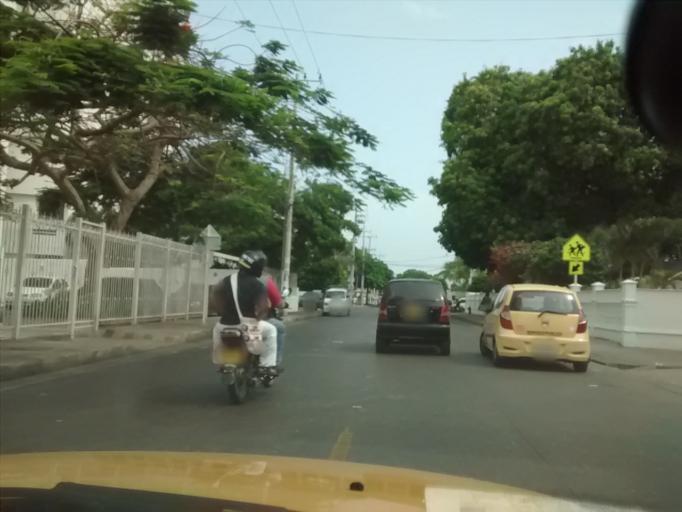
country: CO
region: Bolivar
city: Cartagena
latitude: 10.4140
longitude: -75.5378
